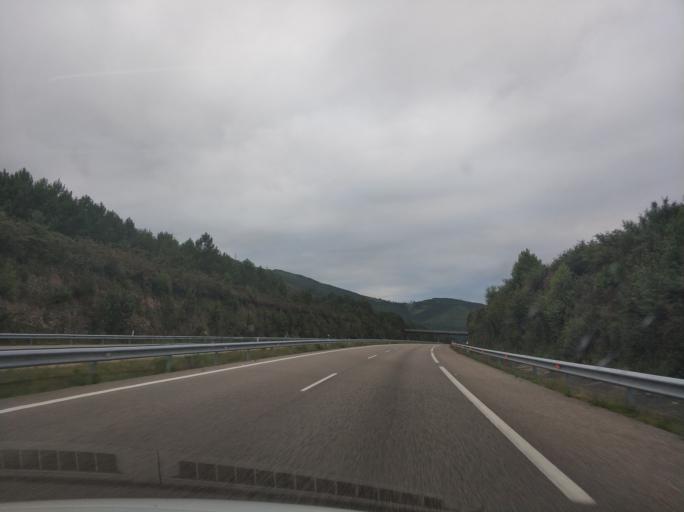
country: ES
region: Asturias
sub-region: Province of Asturias
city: Tineo
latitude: 43.5391
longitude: -6.4774
